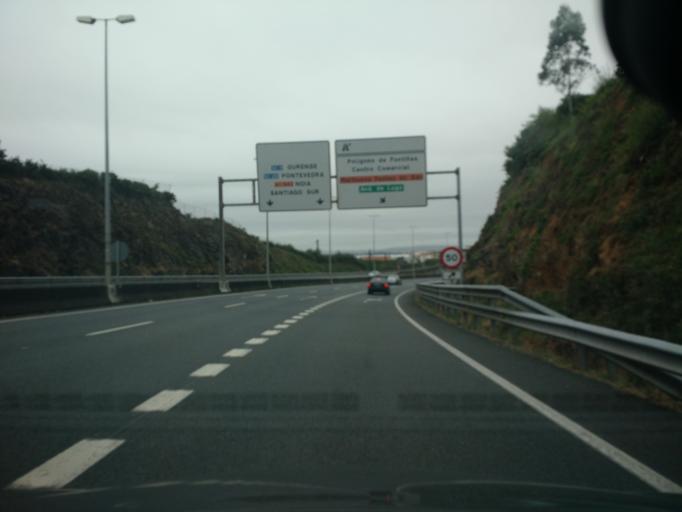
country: ES
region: Galicia
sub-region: Provincia da Coruna
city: Santiago de Compostela
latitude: 42.8795
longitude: -8.5230
